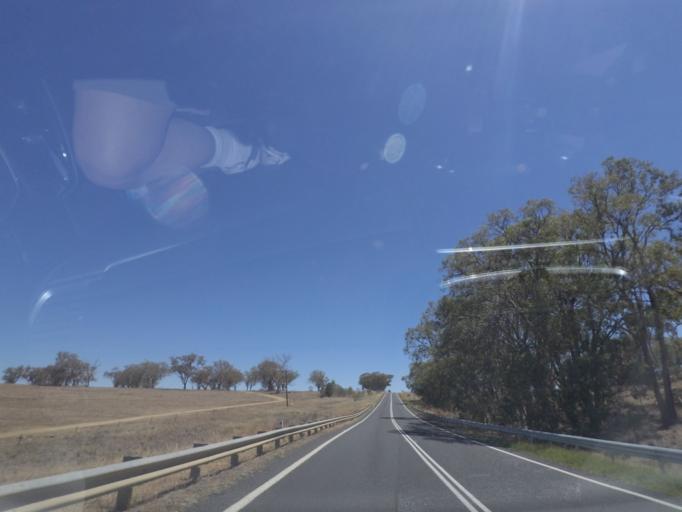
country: AU
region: New South Wales
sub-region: Warrumbungle Shire
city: Coonabarabran
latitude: -31.4261
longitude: 149.1766
